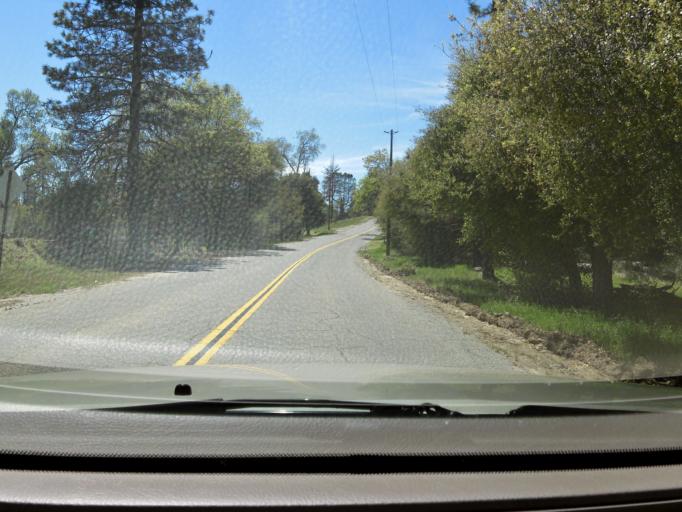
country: US
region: California
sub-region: Madera County
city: Oakhurst
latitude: 37.2411
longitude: -119.5295
